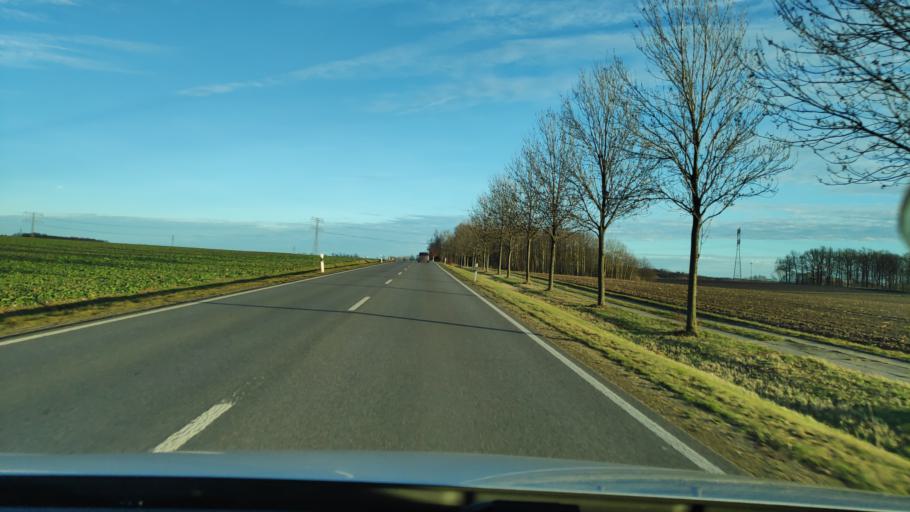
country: DE
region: Saxony
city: Zwickau
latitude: 50.7657
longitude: 12.5114
